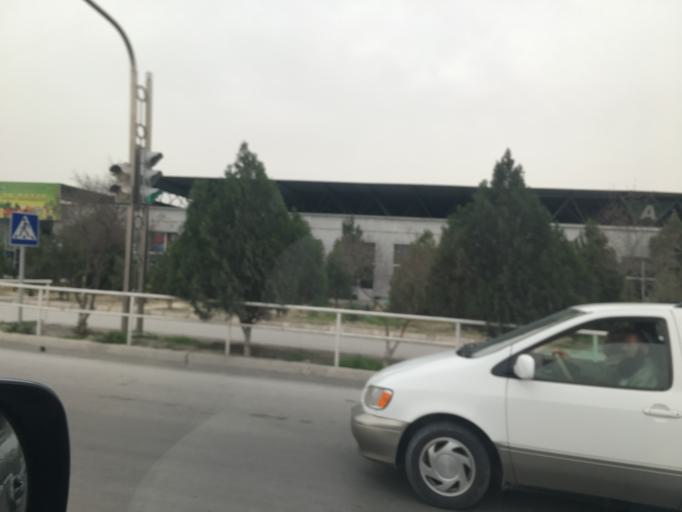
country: TM
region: Ahal
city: Abadan
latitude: 38.1595
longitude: 57.9635
